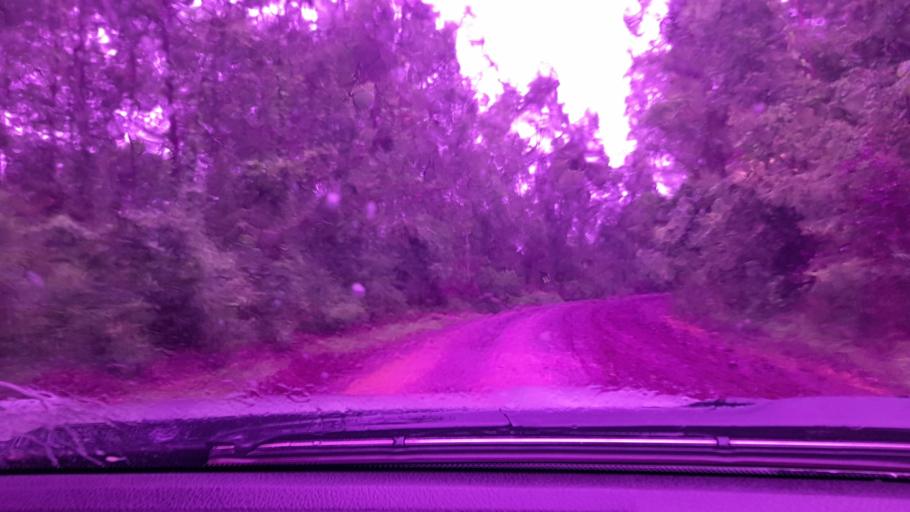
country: ET
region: Oromiya
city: Metu
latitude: 8.3558
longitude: 35.5940
